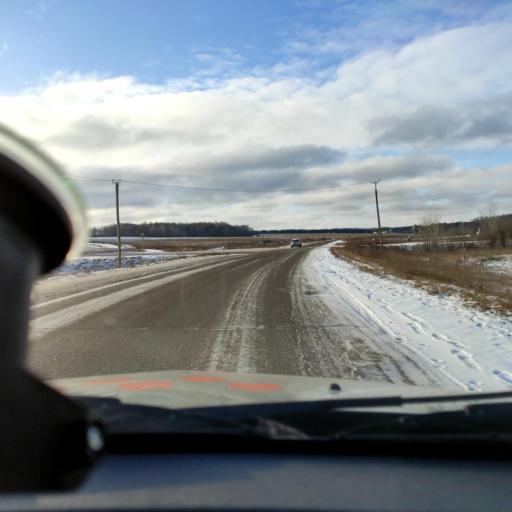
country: RU
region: Bashkortostan
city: Mikhaylovka
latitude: 54.7981
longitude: 55.7797
